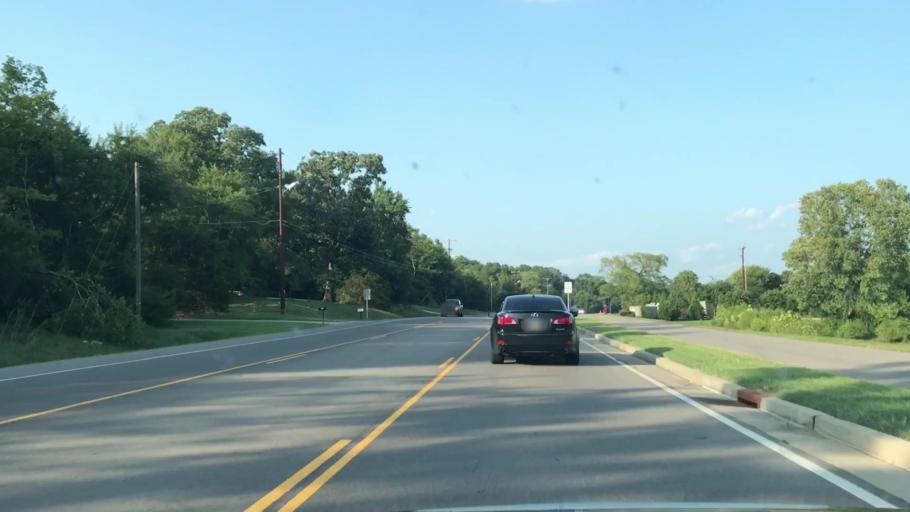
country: US
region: Tennessee
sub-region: Williamson County
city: Nolensville
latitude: 35.9902
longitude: -86.7028
